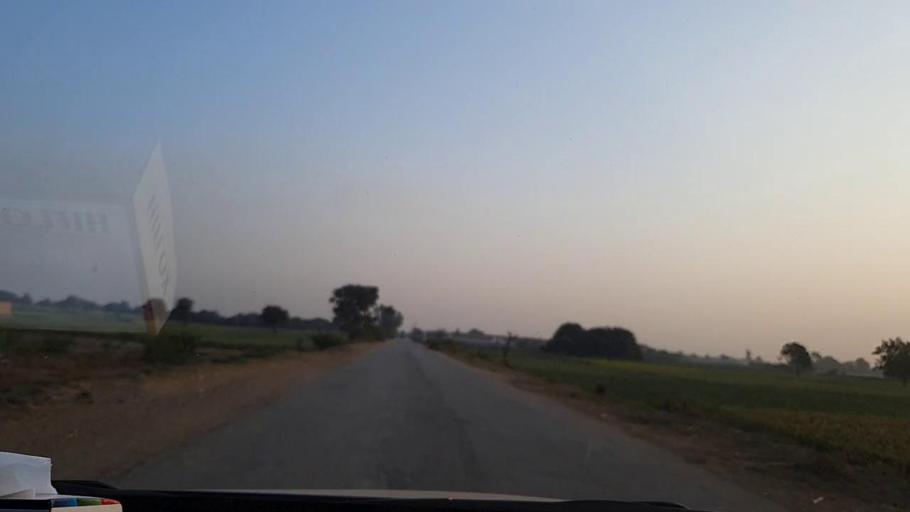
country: PK
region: Sindh
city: Tando Ghulam Ali
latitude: 25.1765
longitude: 68.9490
